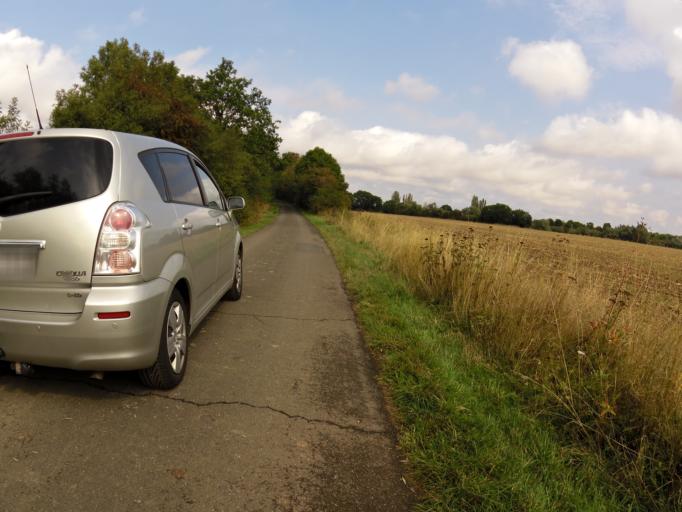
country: DE
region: Lower Saxony
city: Schweringen
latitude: 52.7269
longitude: 9.1958
